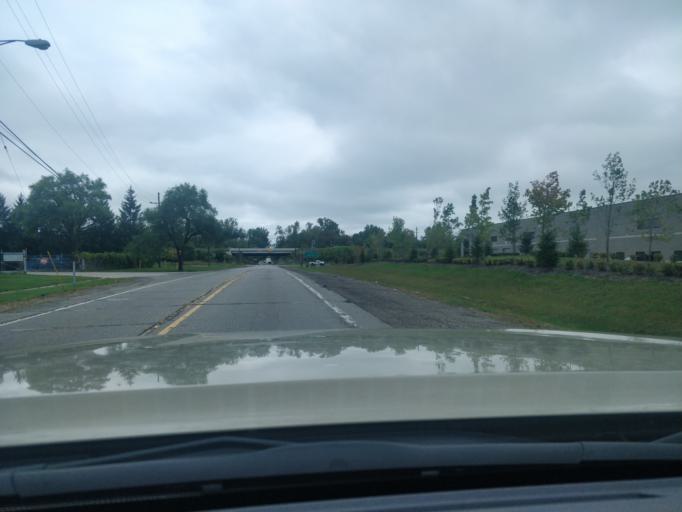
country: US
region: Michigan
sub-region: Wayne County
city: Romulus
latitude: 42.2180
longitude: -83.4244
